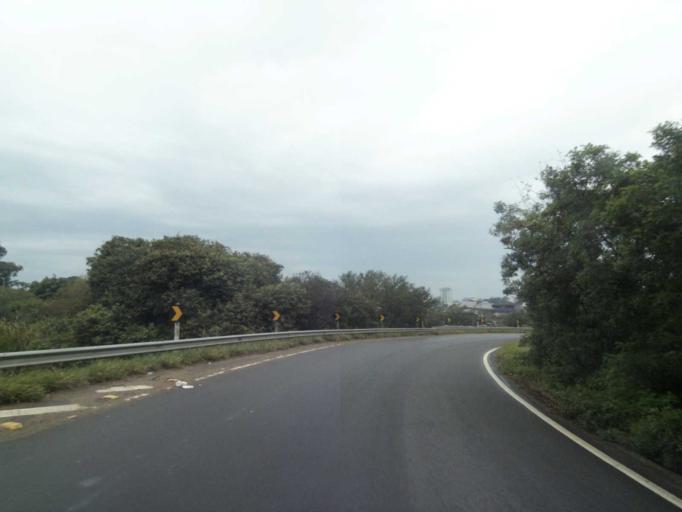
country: BR
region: Rio Grande do Sul
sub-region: Sapucaia Do Sul
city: Sapucaia
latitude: -29.8279
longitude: -51.1714
